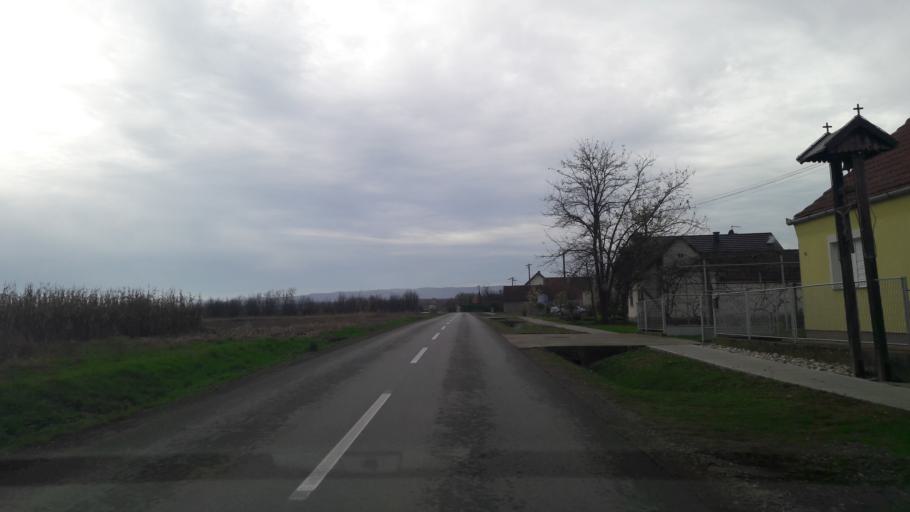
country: HR
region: Osjecko-Baranjska
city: Fericanci
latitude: 45.5273
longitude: 18.0164
